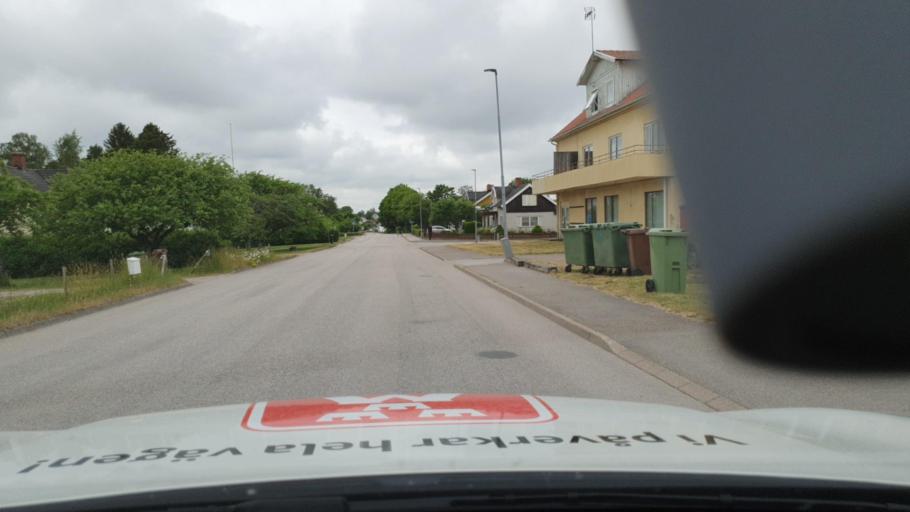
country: SE
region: Vaestra Goetaland
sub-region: Tibro Kommun
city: Tibro
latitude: 58.4040
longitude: 14.1576
